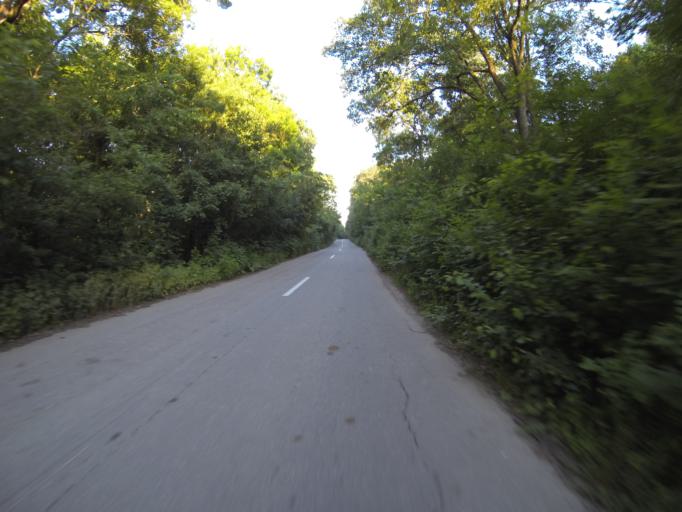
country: RO
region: Dolj
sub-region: Comuna Tuglui
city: Tuglui
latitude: 44.1733
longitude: 23.8187
